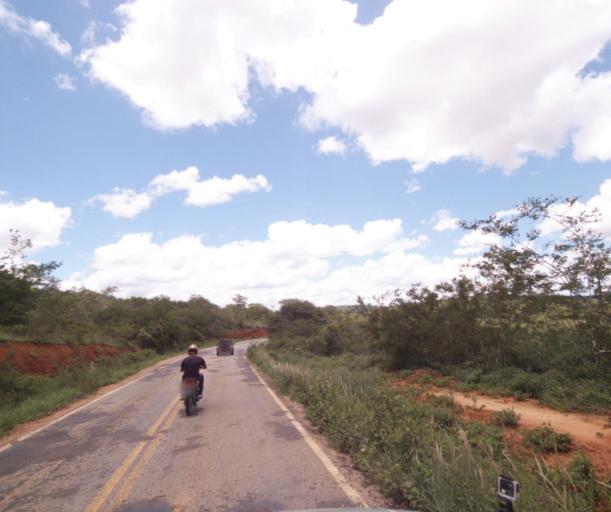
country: BR
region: Bahia
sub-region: Pocoes
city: Pocoes
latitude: -14.3884
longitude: -40.5202
